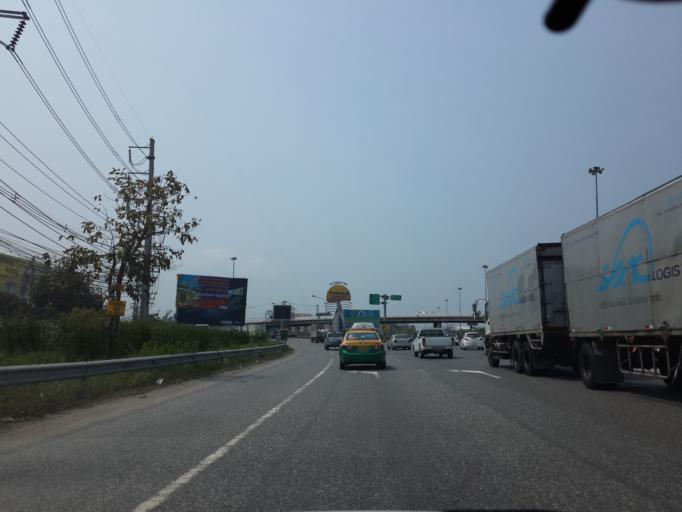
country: TH
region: Chon Buri
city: Chon Buri
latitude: 13.4217
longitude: 100.9982
